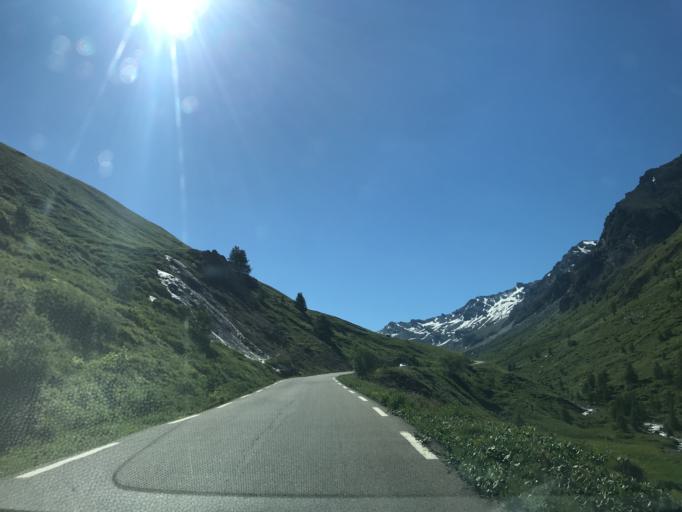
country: IT
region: Piedmont
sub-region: Provincia di Cuneo
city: Pontechianale
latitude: 44.7035
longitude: 6.9355
